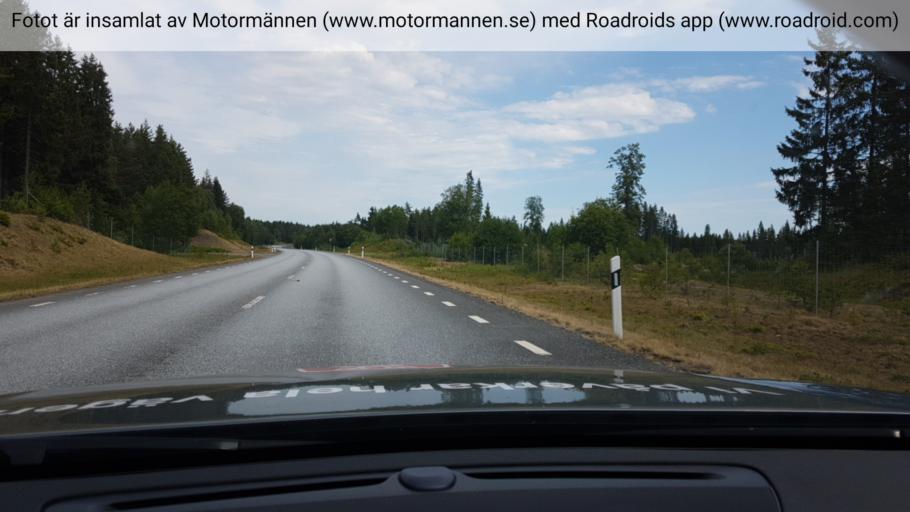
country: SE
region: Uppsala
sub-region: Osthammars Kommun
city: Gimo
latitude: 60.1684
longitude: 18.2831
